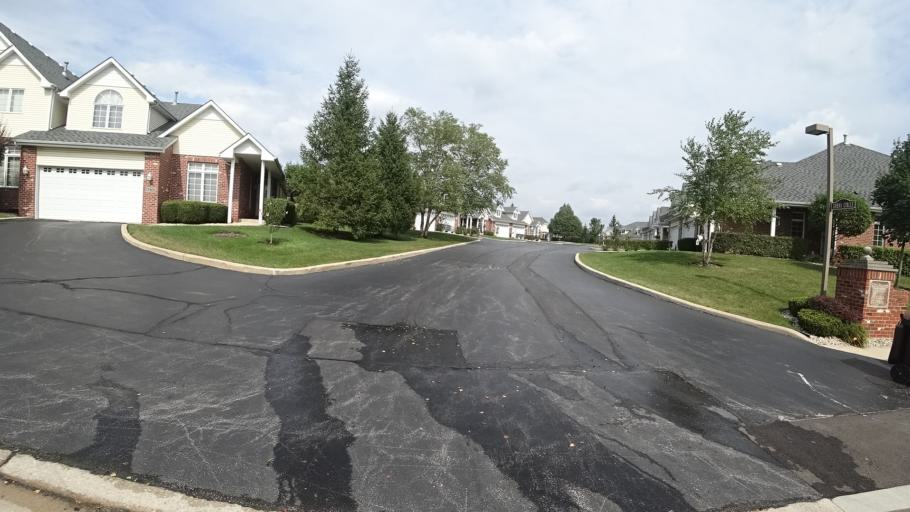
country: US
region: Illinois
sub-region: Cook County
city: Tinley Park
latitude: 41.5989
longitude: -87.7882
